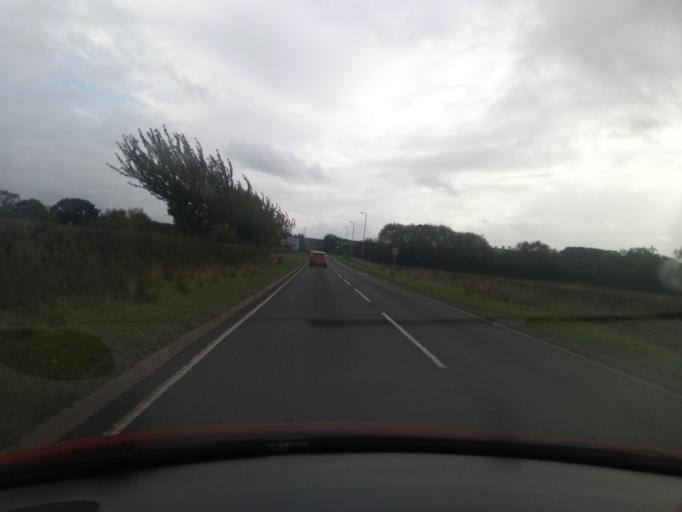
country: GB
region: England
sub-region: Nottinghamshire
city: Cotgrave
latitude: 52.9203
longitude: -1.0141
